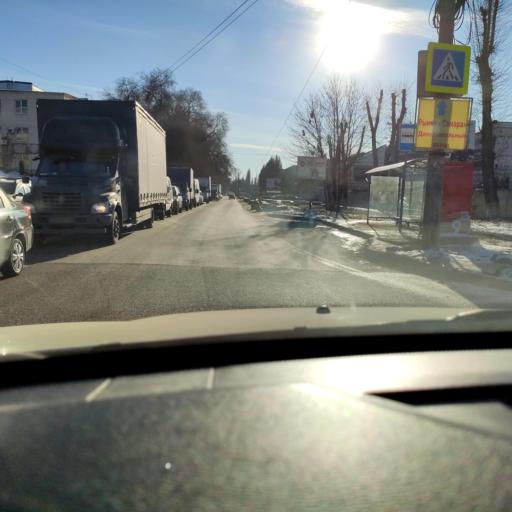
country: RU
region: Samara
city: Samara
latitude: 53.1945
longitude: 50.2457
